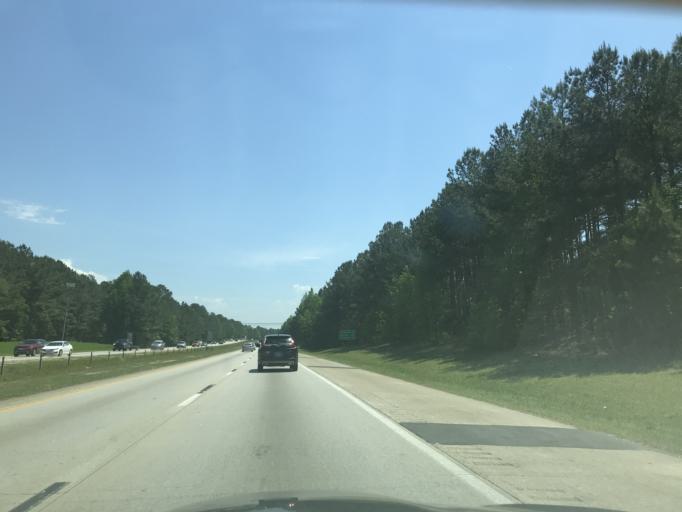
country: US
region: North Carolina
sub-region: Wake County
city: Garner
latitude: 35.6841
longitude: -78.5691
